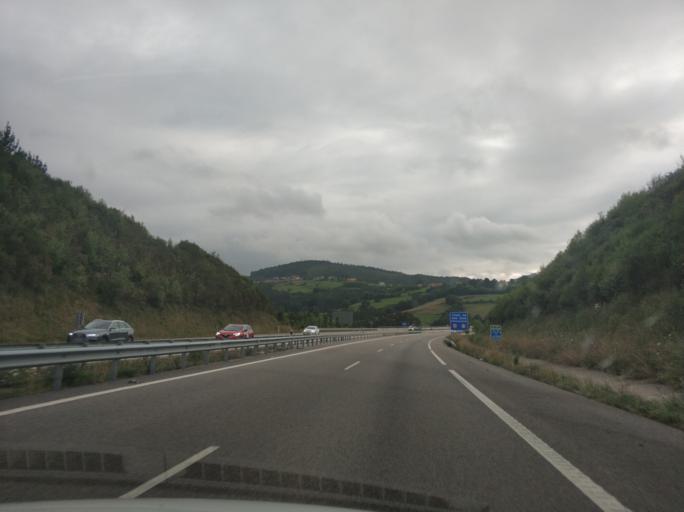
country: ES
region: Asturias
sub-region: Province of Asturias
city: Cudillero
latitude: 43.5434
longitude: -6.1437
